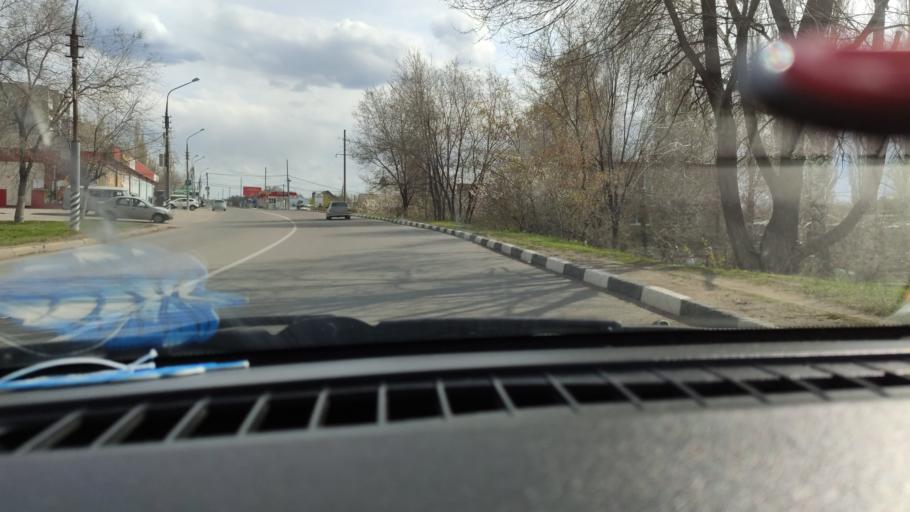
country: RU
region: Saratov
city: Privolzhskiy
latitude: 51.3905
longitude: 46.0357
